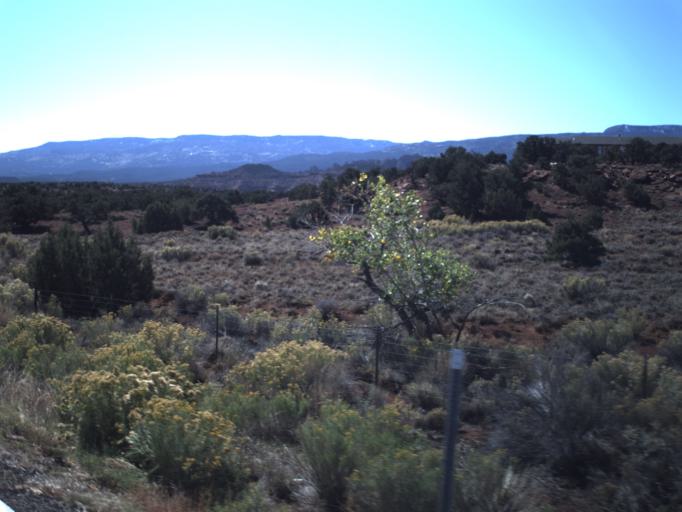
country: US
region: Utah
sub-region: Wayne County
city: Loa
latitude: 38.2919
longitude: -111.3965
